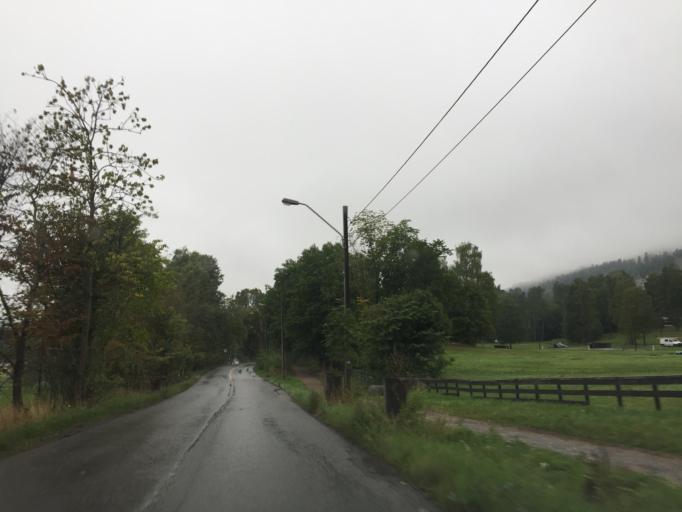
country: NO
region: Akershus
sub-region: Baerum
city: Lysaker
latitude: 59.9634
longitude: 10.6396
